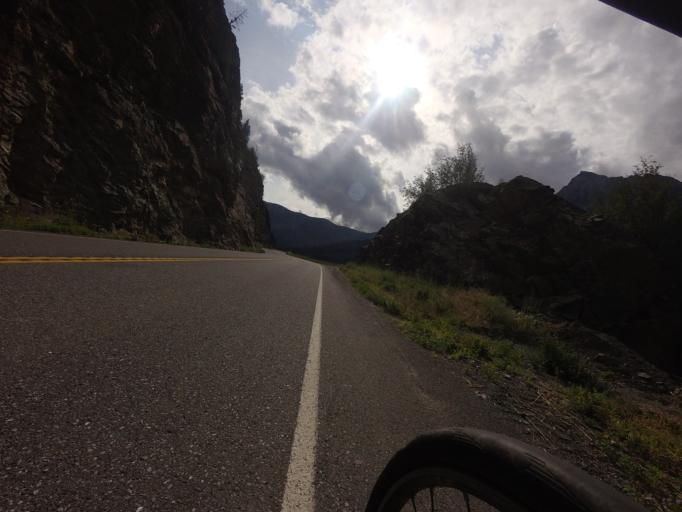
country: CA
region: British Columbia
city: Lillooet
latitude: 50.6415
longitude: -122.0406
